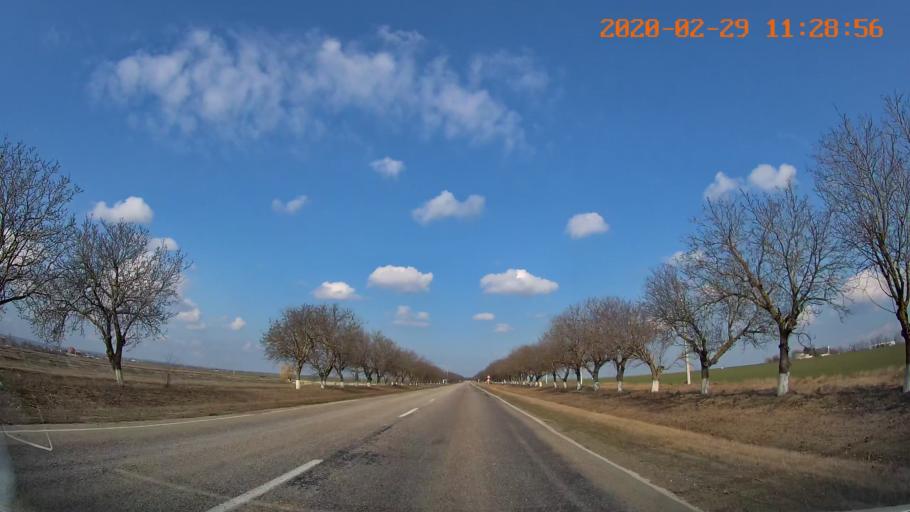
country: MD
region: Telenesti
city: Cocieri
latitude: 47.4868
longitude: 29.1298
